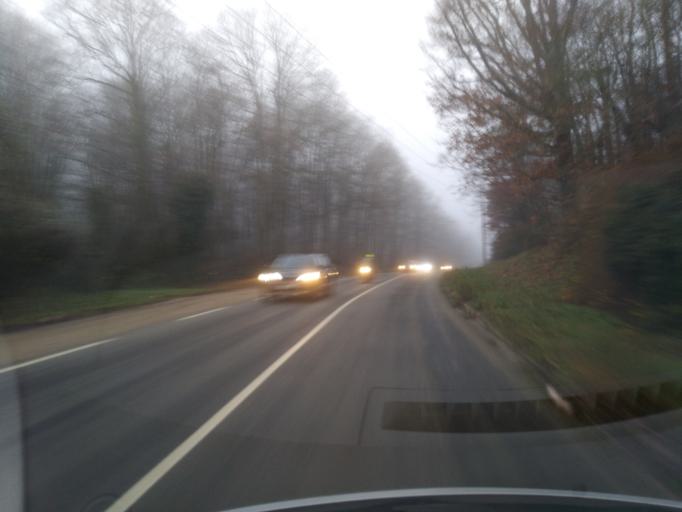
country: FR
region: Ile-de-France
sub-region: Departement des Yvelines
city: Orgeval
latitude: 48.9172
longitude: 1.9634
